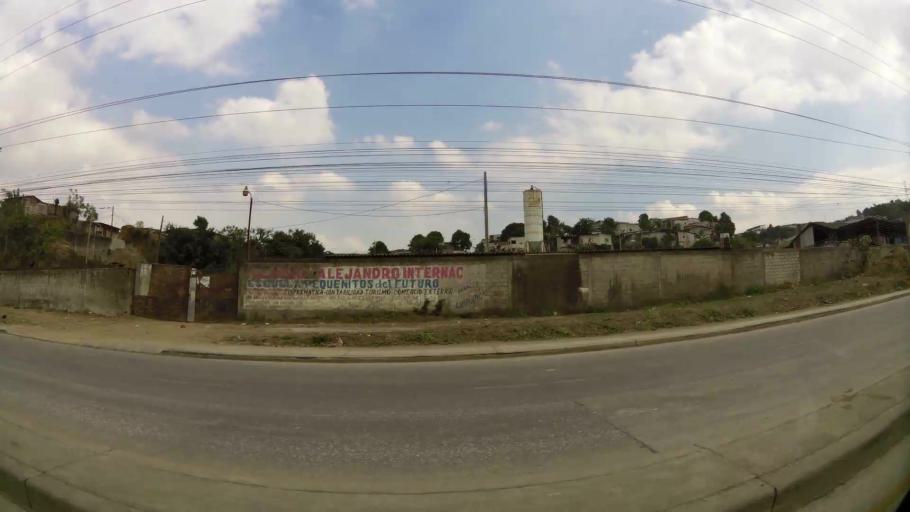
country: EC
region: Guayas
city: Santa Lucia
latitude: -2.1189
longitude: -79.9596
